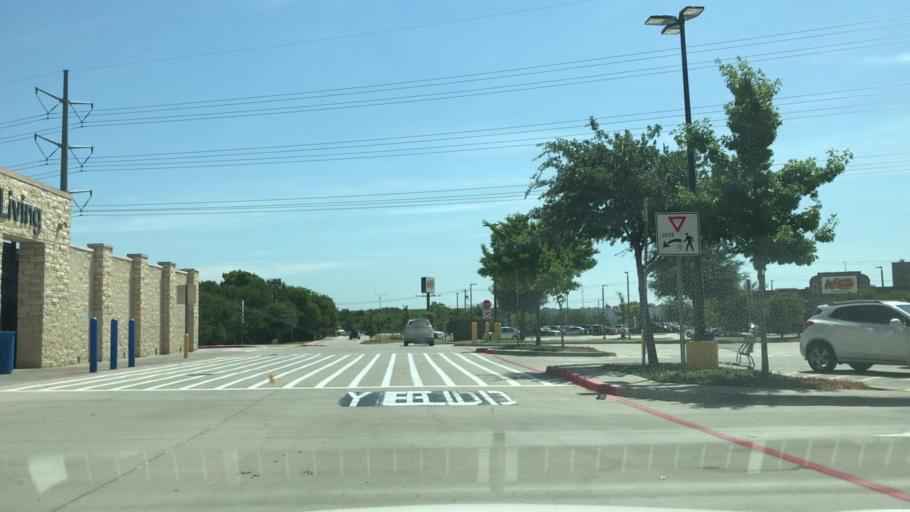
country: US
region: Texas
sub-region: Collin County
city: Allen
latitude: 33.1191
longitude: -96.6717
